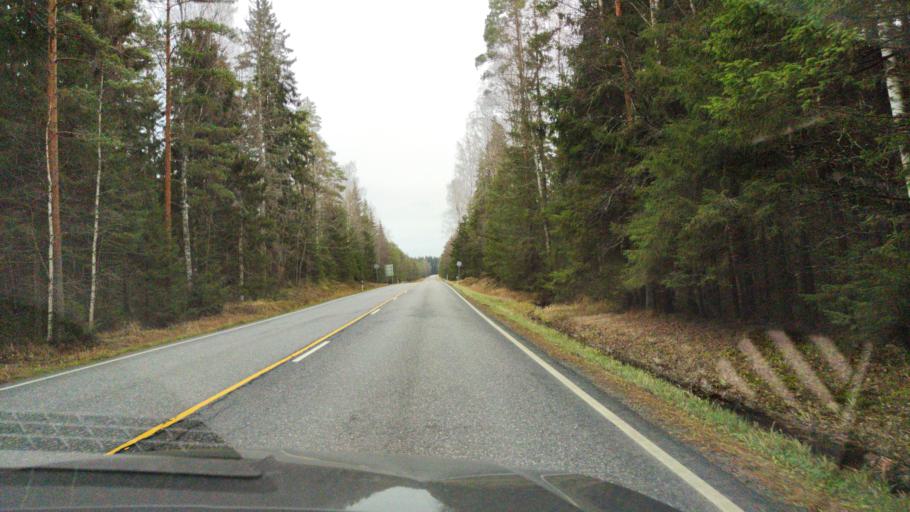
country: FI
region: Varsinais-Suomi
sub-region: Loimaa
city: Ylaene
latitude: 60.7446
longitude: 22.4263
